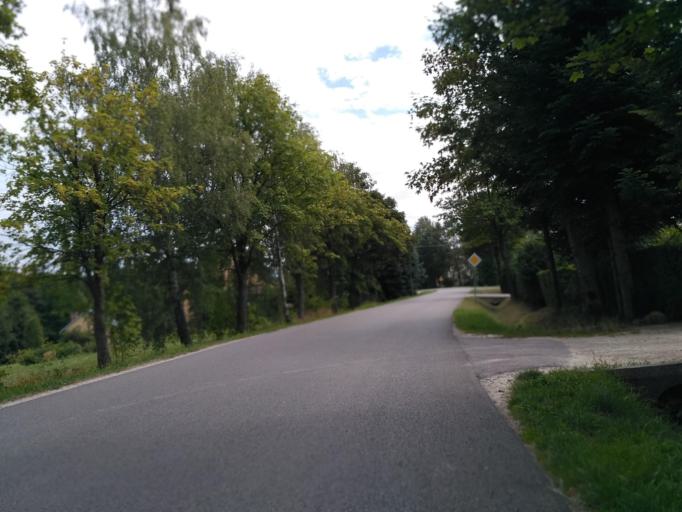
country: PL
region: Subcarpathian Voivodeship
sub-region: Powiat rzeszowski
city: Chmielnik
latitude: 49.9530
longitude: 22.1363
